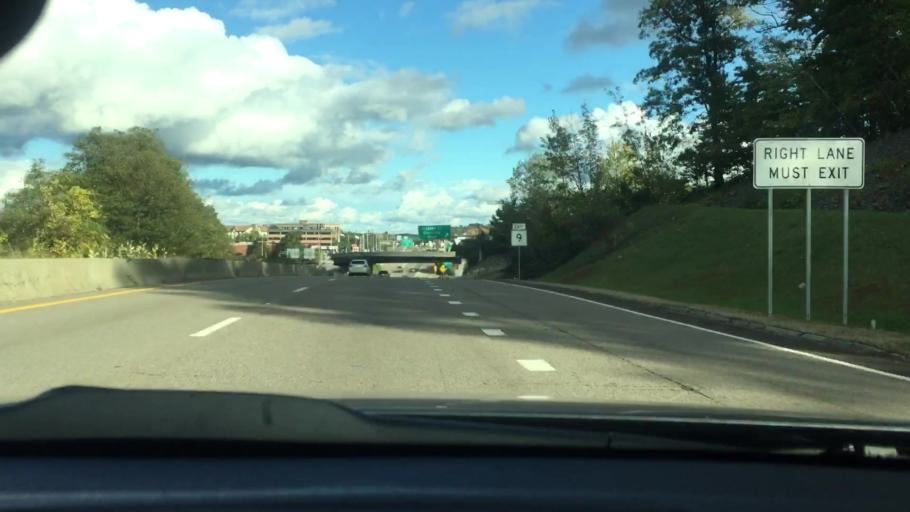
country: US
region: Massachusetts
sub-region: Worcester County
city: Southborough
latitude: 42.2971
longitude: -71.4894
